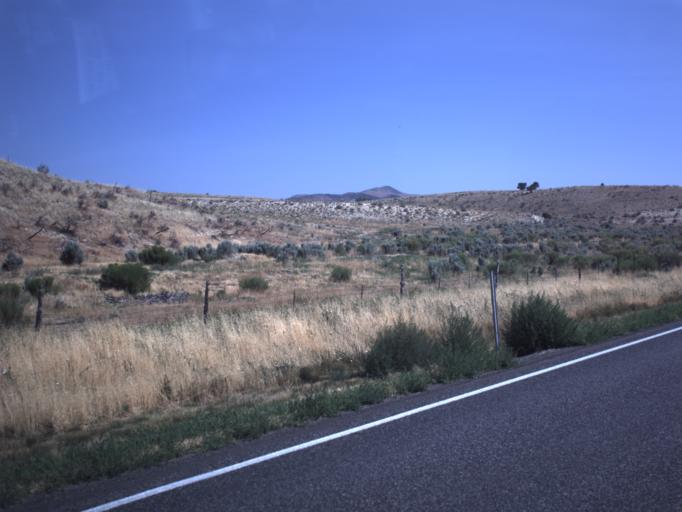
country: US
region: Utah
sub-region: Sanpete County
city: Moroni
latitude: 39.5342
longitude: -111.5416
